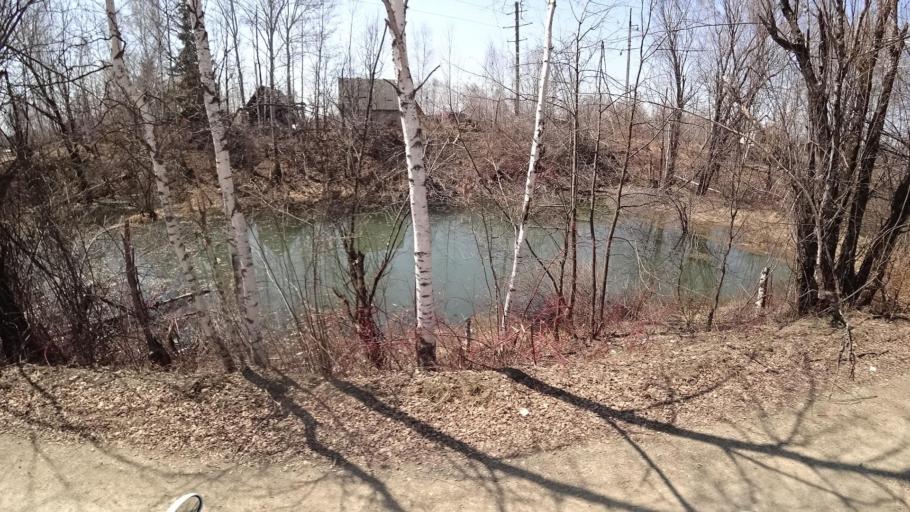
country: RU
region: Khabarovsk Krai
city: Khurba
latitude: 50.4132
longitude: 136.8723
